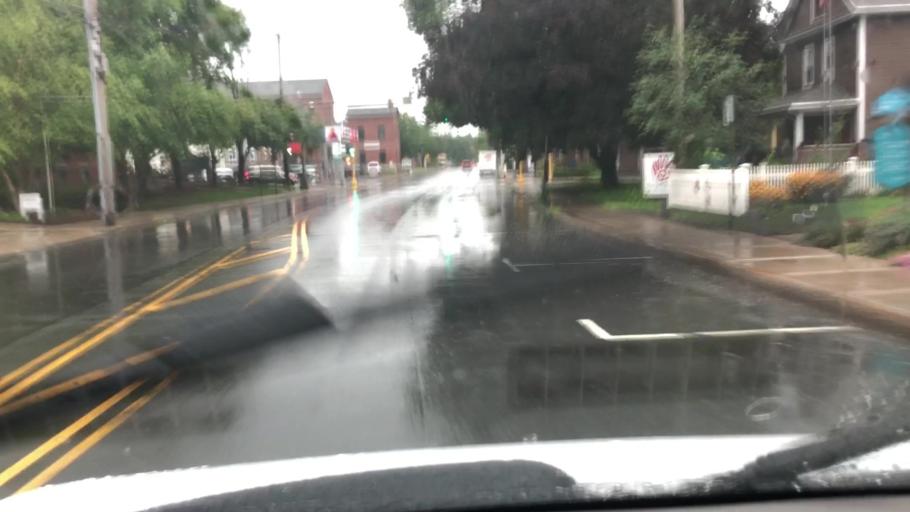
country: US
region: Massachusetts
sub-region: Hampshire County
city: Northampton
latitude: 42.3347
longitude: -72.6668
